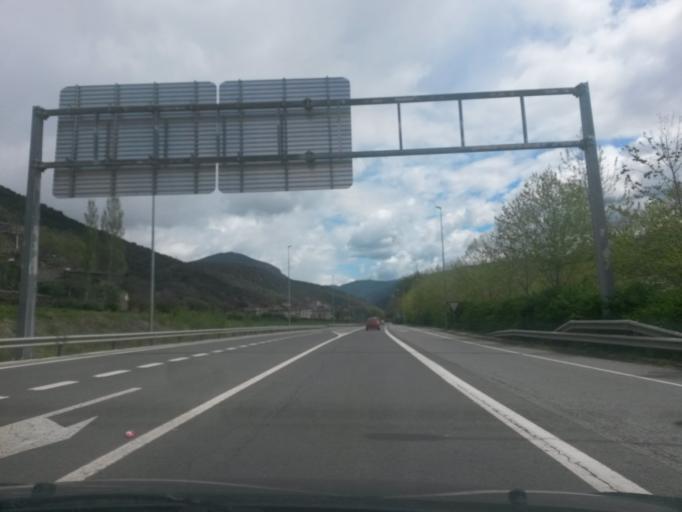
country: ES
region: Catalonia
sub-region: Provincia de Lleida
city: la Seu d'Urgell
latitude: 42.3614
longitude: 1.4675
